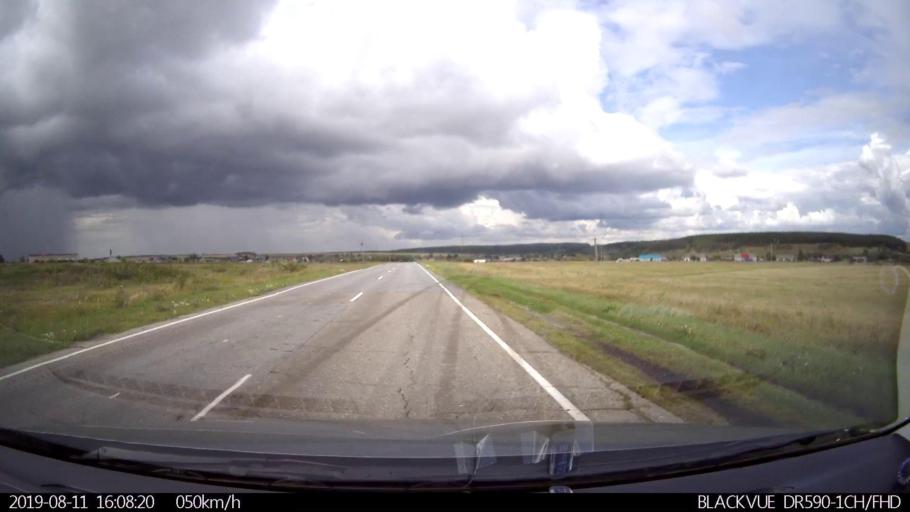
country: RU
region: Ulyanovsk
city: Ignatovka
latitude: 53.9838
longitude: 47.6478
